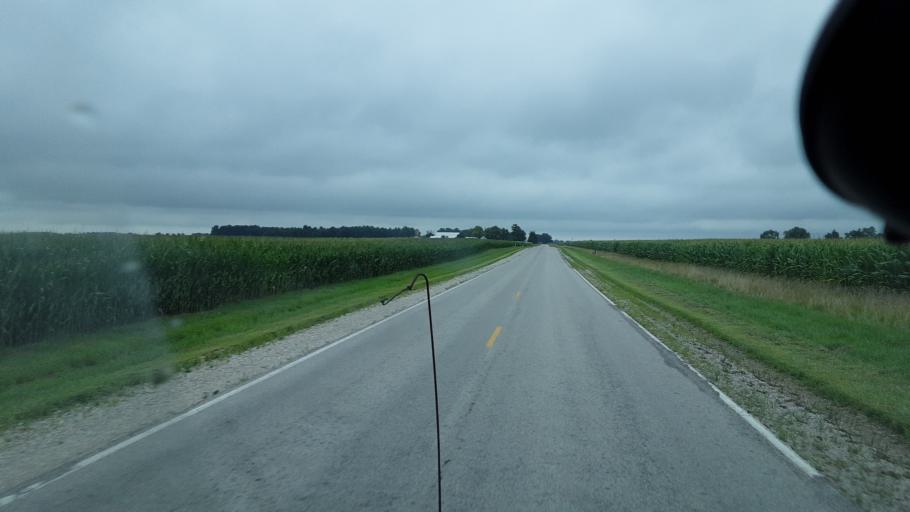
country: US
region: Indiana
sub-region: Wells County
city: Ossian
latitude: 40.8083
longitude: -85.0906
